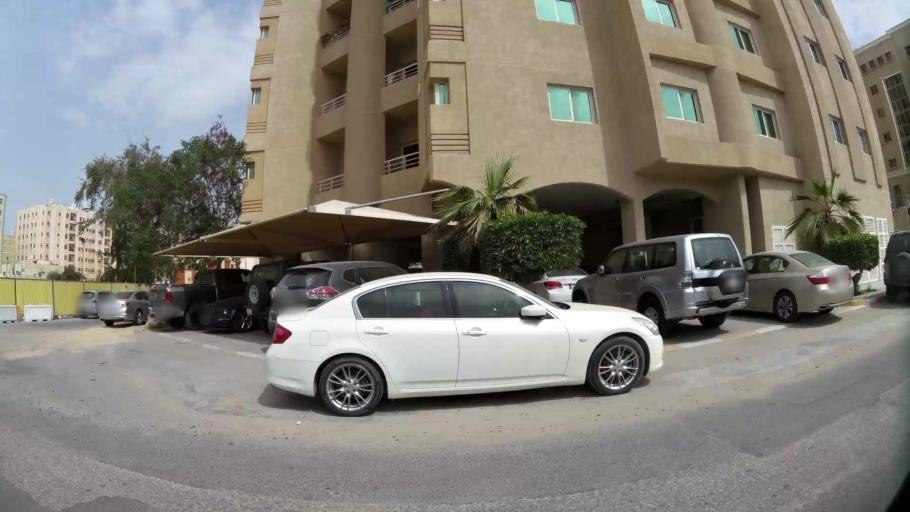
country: QA
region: Baladiyat ad Dawhah
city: Doha
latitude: 25.2846
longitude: 51.4994
